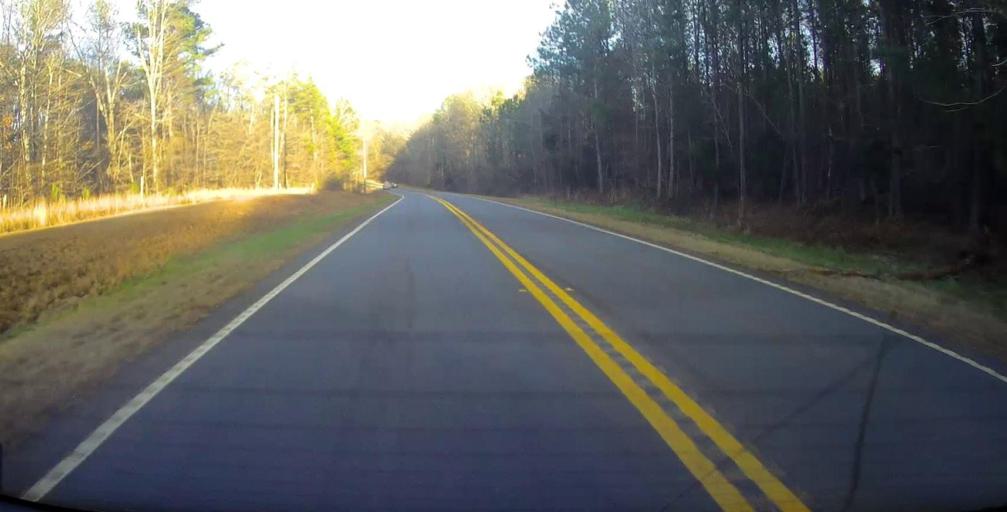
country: US
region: Georgia
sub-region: Talbot County
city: Sardis
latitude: 32.7441
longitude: -84.5995
